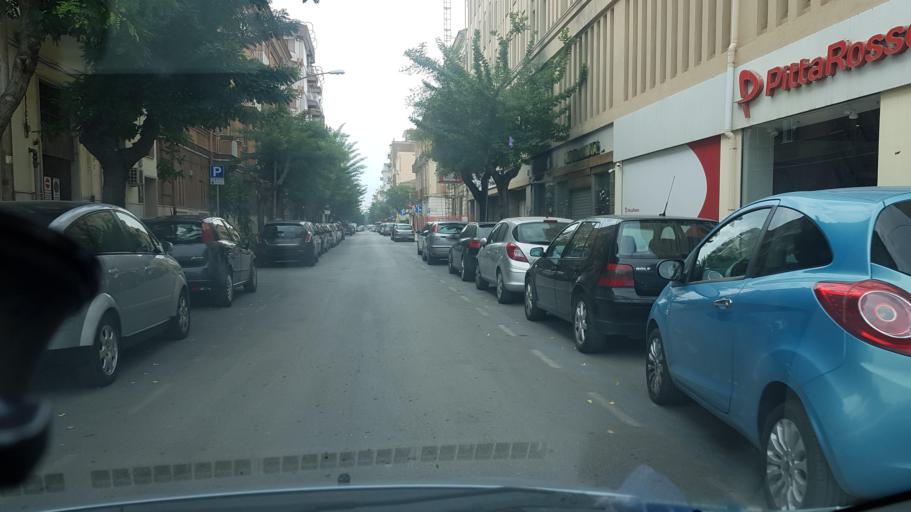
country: IT
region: Apulia
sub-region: Provincia di Foggia
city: Foggia
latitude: 41.4611
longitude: 15.5530
